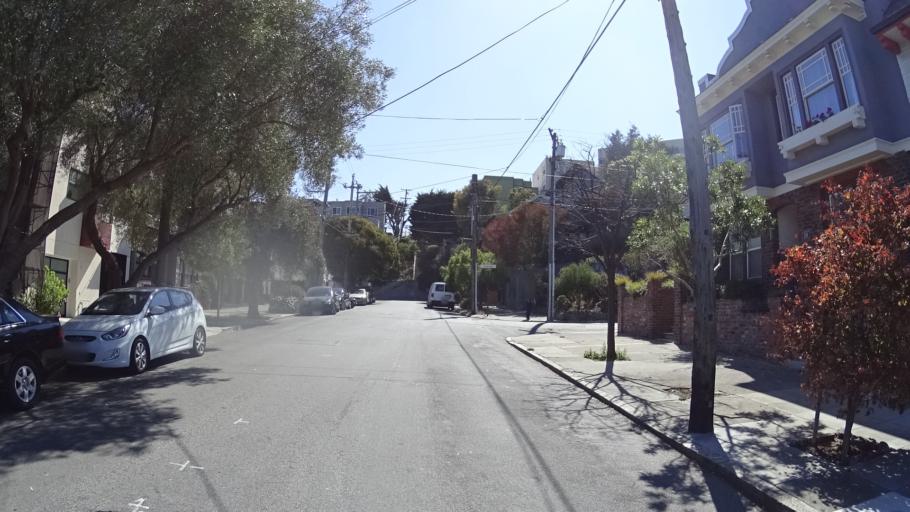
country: US
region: California
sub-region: San Francisco County
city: San Francisco
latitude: 37.7581
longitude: -122.4391
